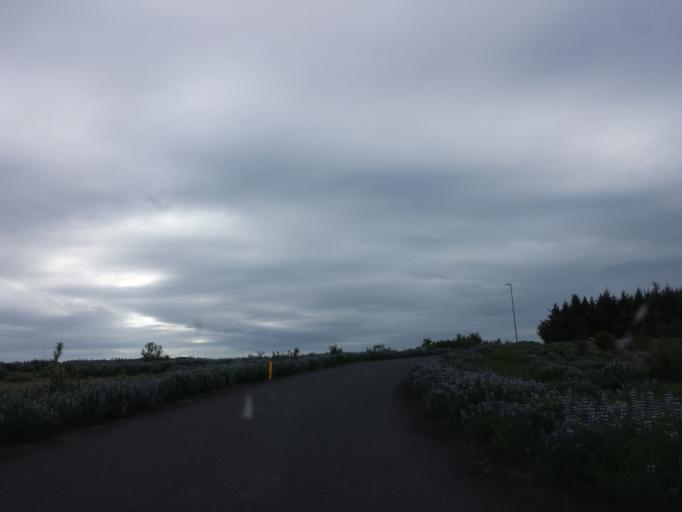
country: IS
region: Capital Region
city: Alftanes
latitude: 64.0874
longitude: -21.9851
